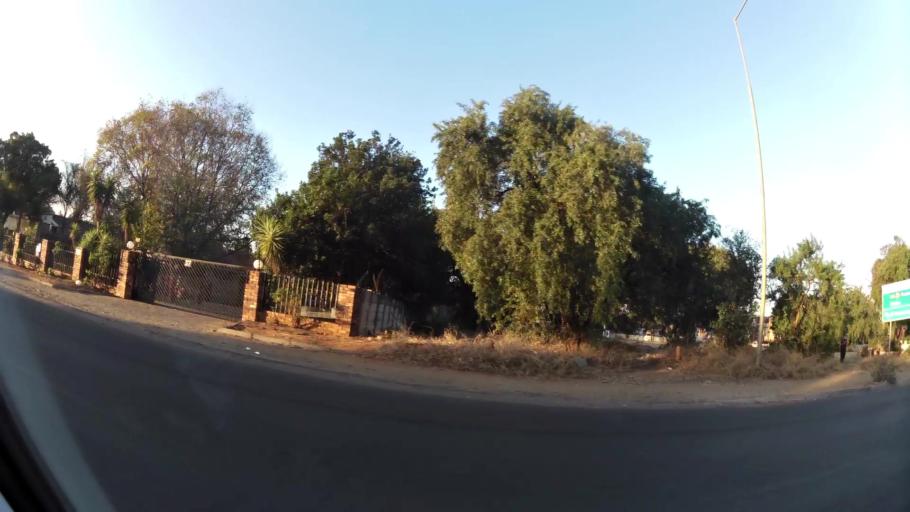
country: ZA
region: North-West
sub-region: Bojanala Platinum District Municipality
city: Rustenburg
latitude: -25.6853
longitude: 27.2248
